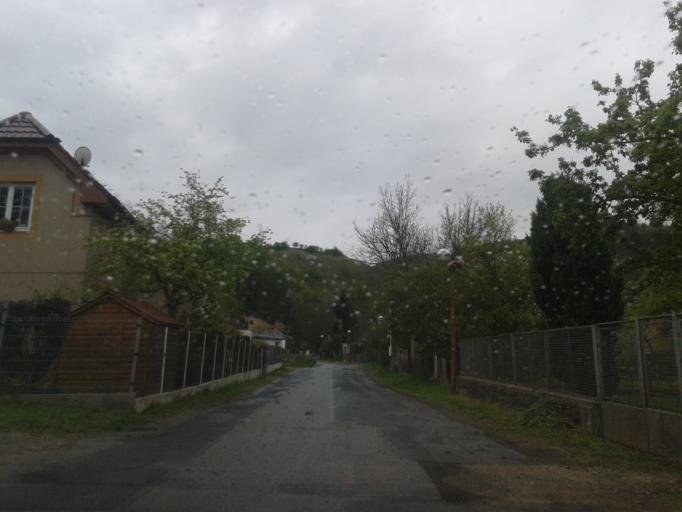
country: CZ
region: Central Bohemia
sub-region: Okres Beroun
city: Lodenice
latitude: 49.9359
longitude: 14.1354
